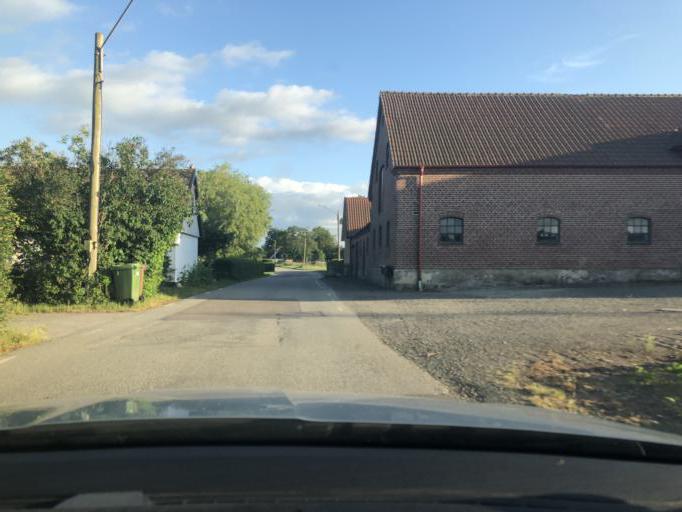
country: SE
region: Skane
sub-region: Simrishamns Kommun
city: Simrishamn
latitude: 55.4992
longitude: 14.2033
